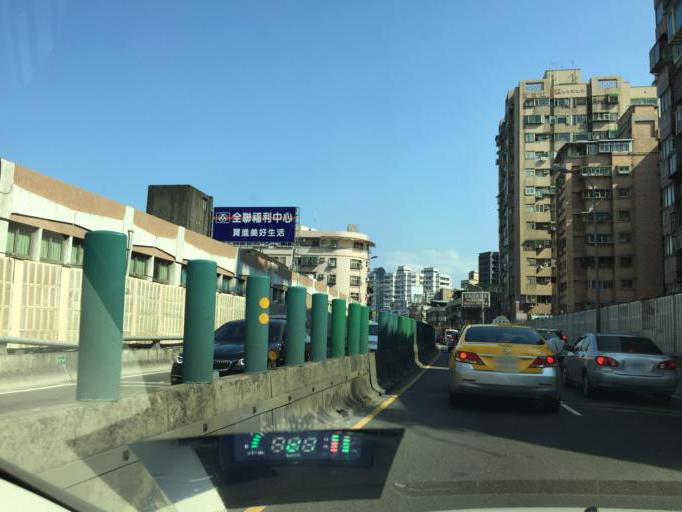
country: TW
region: Taipei
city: Taipei
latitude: 25.0572
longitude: 121.4911
